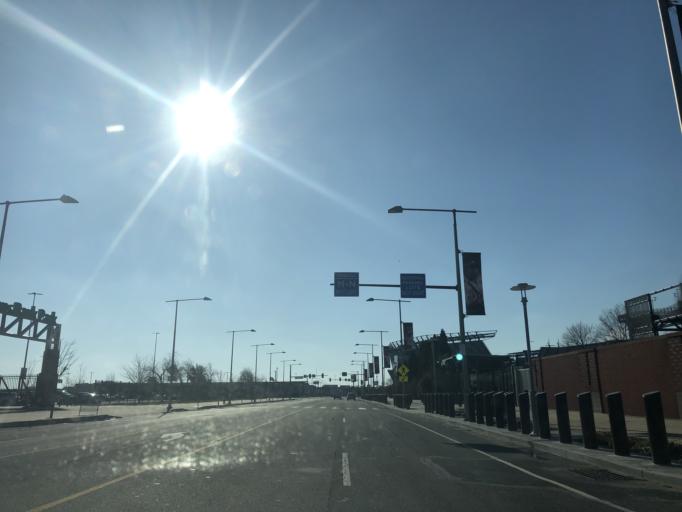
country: US
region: New Jersey
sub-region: Gloucester County
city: National Park
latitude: 39.9059
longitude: -75.1643
